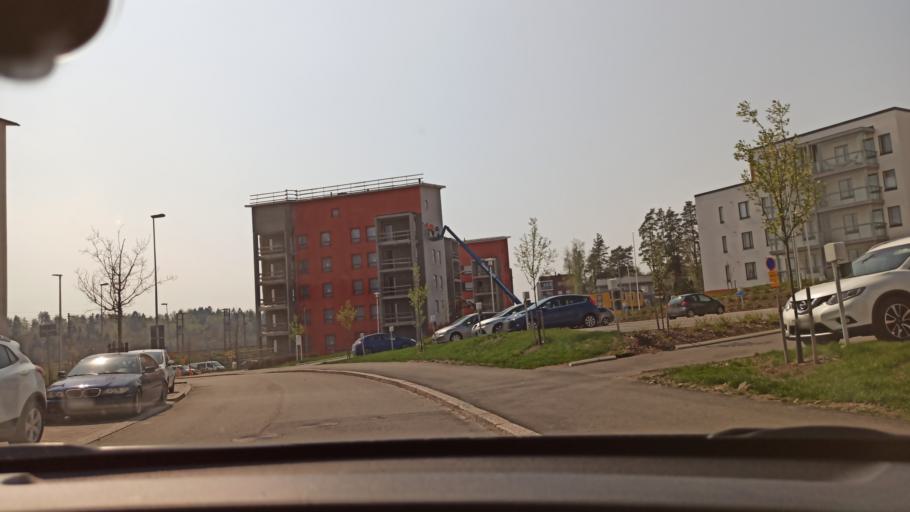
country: FI
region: Uusimaa
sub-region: Helsinki
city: Kirkkonummi
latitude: 60.1212
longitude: 24.4765
